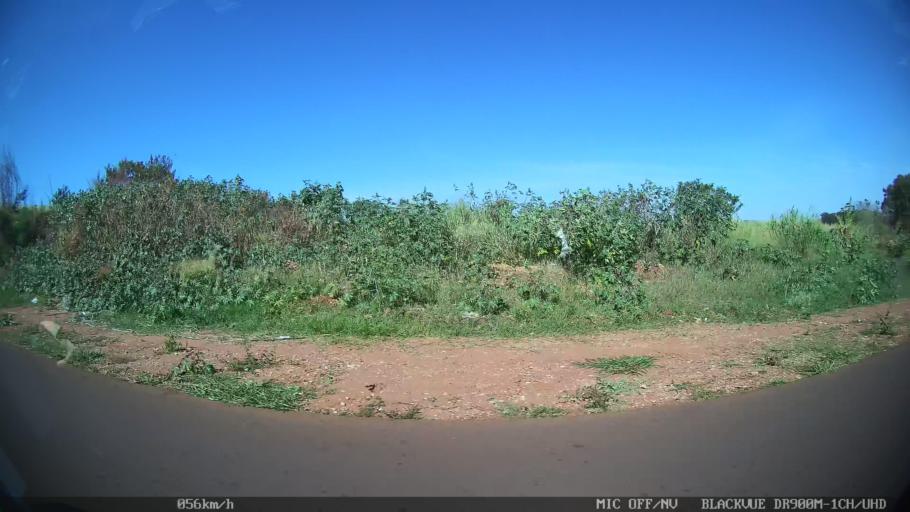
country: BR
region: Sao Paulo
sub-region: Batatais
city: Batatais
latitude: -20.8755
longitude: -47.5848
